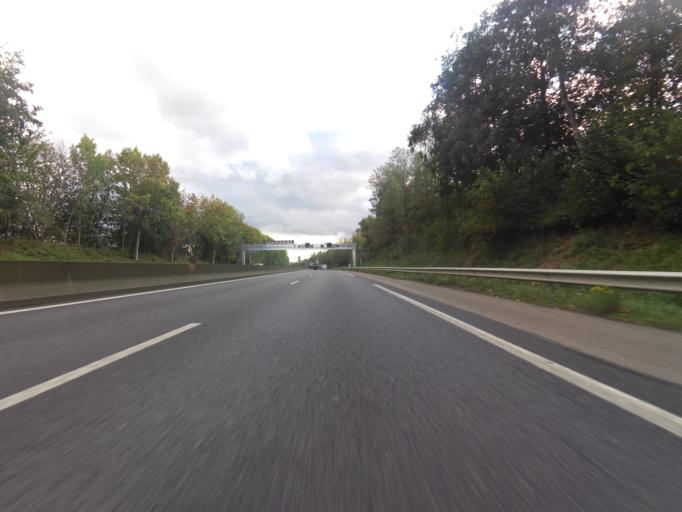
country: FR
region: Haute-Normandie
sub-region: Departement de la Seine-Maritime
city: Bois-Guillaume
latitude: 49.4727
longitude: 1.1345
